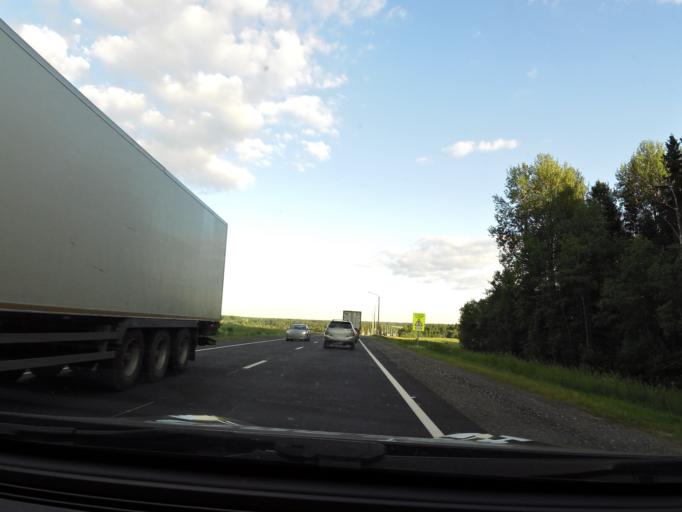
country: RU
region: Vologda
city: Gryazovets
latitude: 59.0384
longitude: 40.1063
